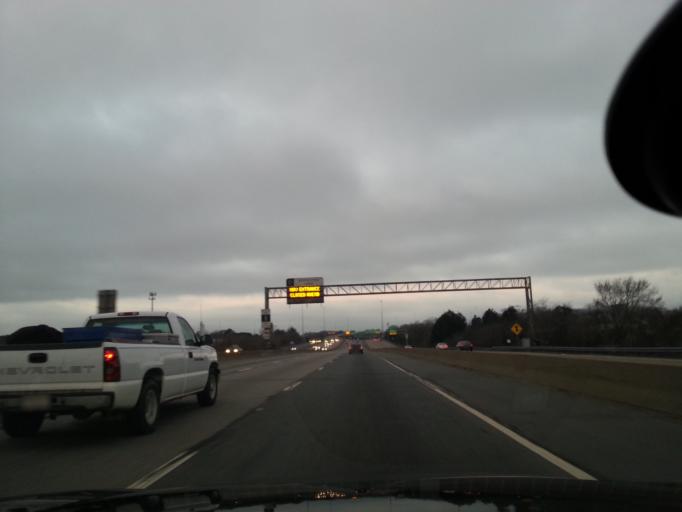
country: US
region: Virginia
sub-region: City of Chesapeake
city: Chesapeake
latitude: 36.8460
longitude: -76.1838
